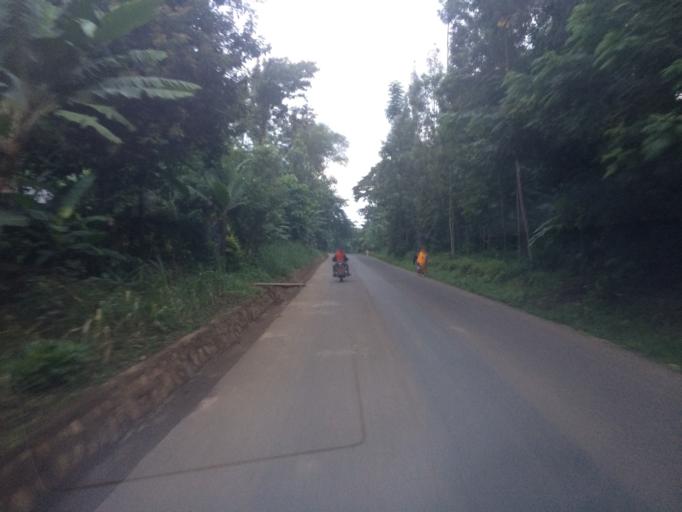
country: TZ
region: Arusha
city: Nkoaranga
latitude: -3.3507
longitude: 36.8138
